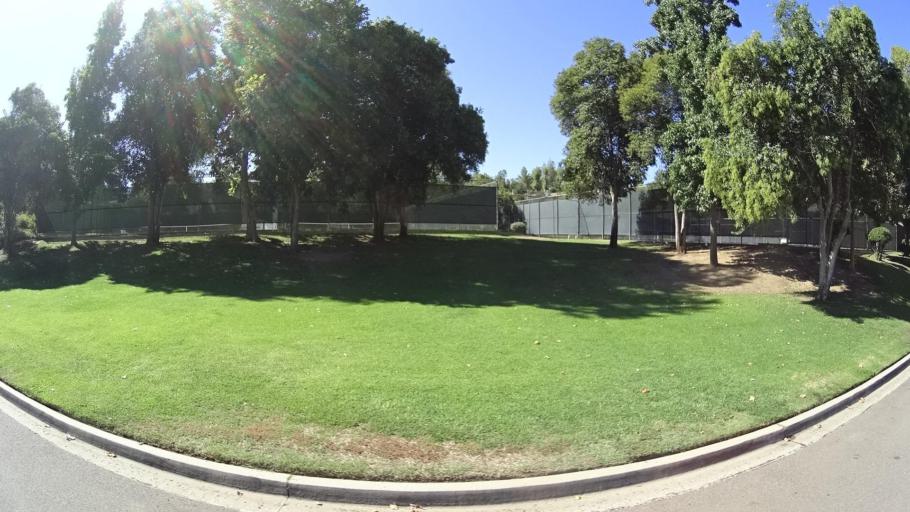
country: US
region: California
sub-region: San Diego County
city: San Diego Country Estates
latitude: 33.0037
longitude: -116.7787
